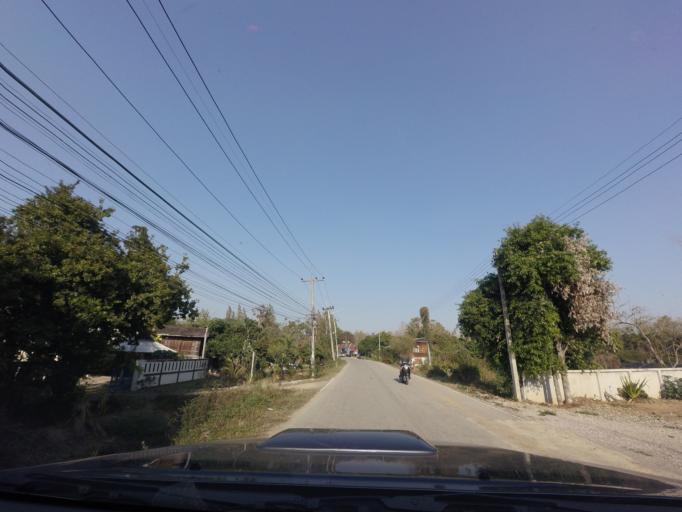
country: TH
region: Chiang Mai
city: San Sai
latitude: 18.9342
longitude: 98.9707
